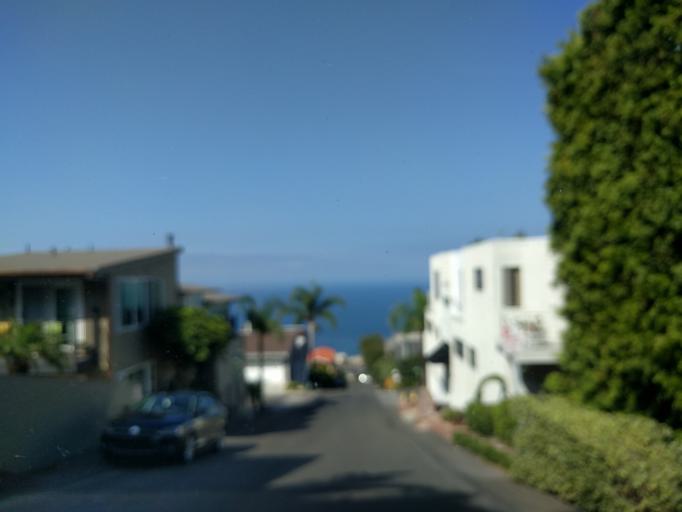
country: US
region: California
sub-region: Orange County
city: Laguna Beach
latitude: 33.5307
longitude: -117.7613
